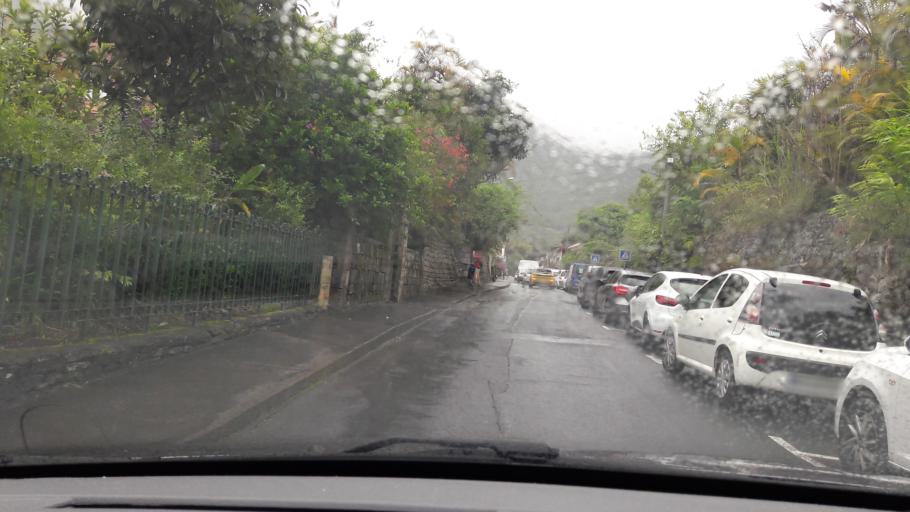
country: RE
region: Reunion
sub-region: Reunion
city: Salazie
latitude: -21.0649
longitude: 55.5204
